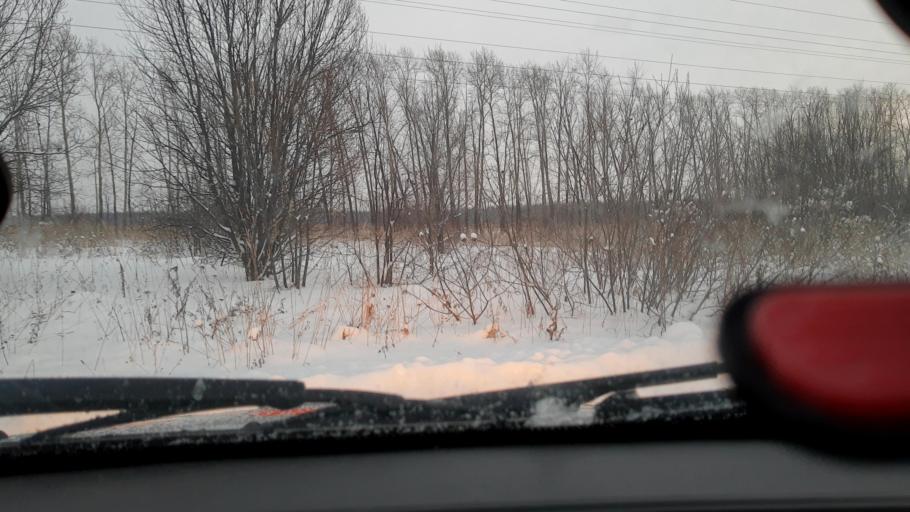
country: RU
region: Bashkortostan
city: Iglino
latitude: 54.7308
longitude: 56.2350
